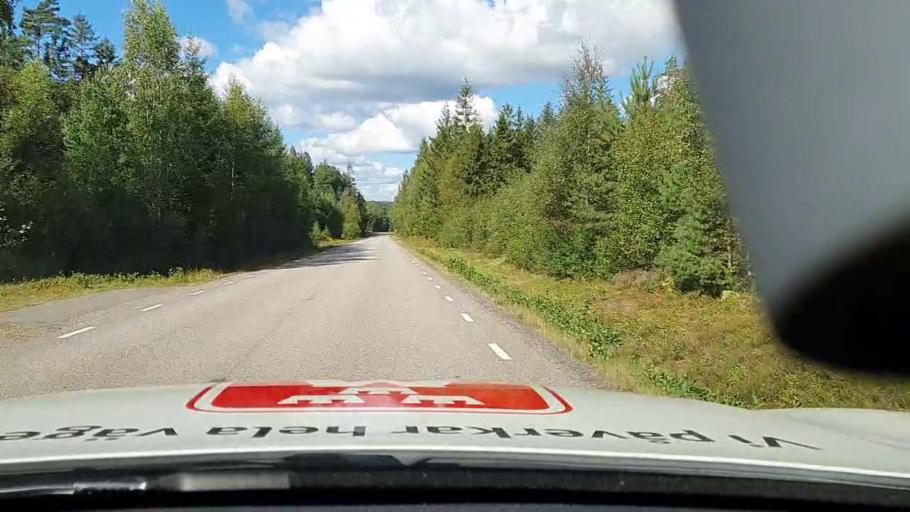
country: SE
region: Vaestra Goetaland
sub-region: Marks Kommun
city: Fritsla
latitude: 57.3905
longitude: 12.8538
